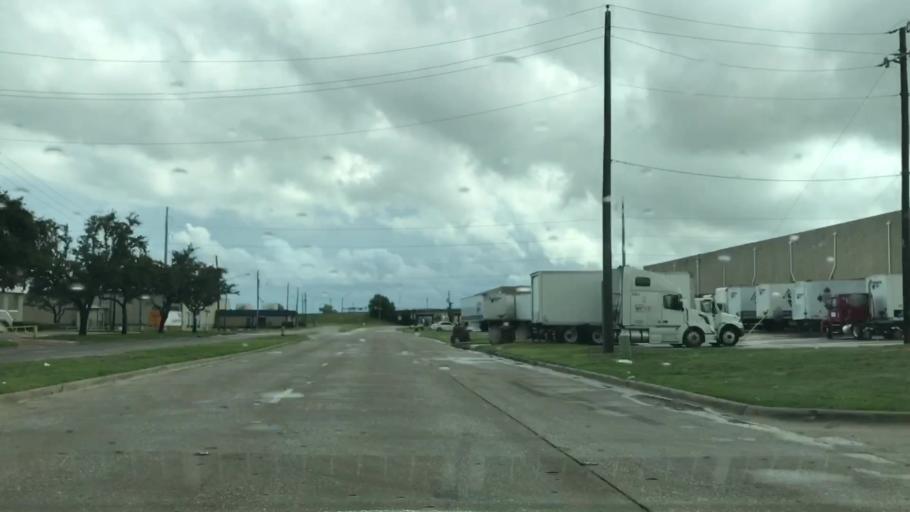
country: US
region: Texas
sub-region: Dallas County
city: Irving
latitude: 32.8116
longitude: -96.9002
